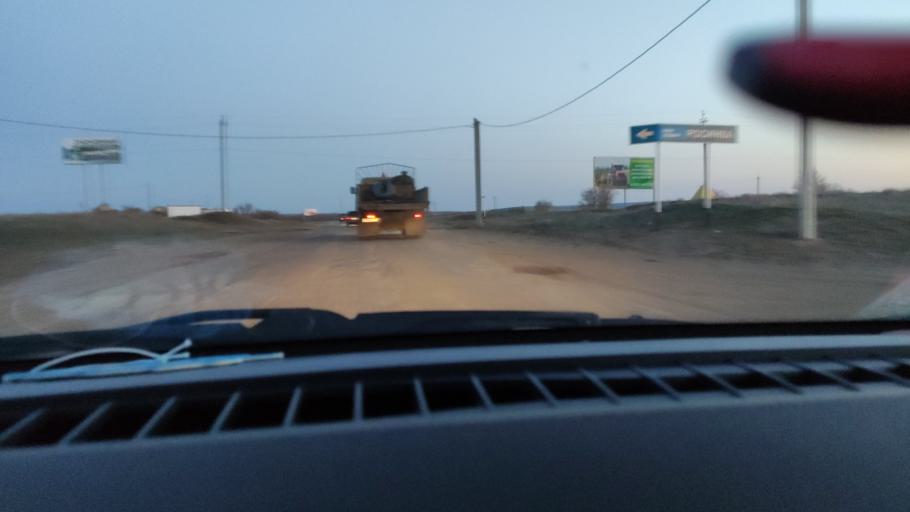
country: RU
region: Saratov
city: Rovnoye
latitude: 51.0184
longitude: 46.0941
